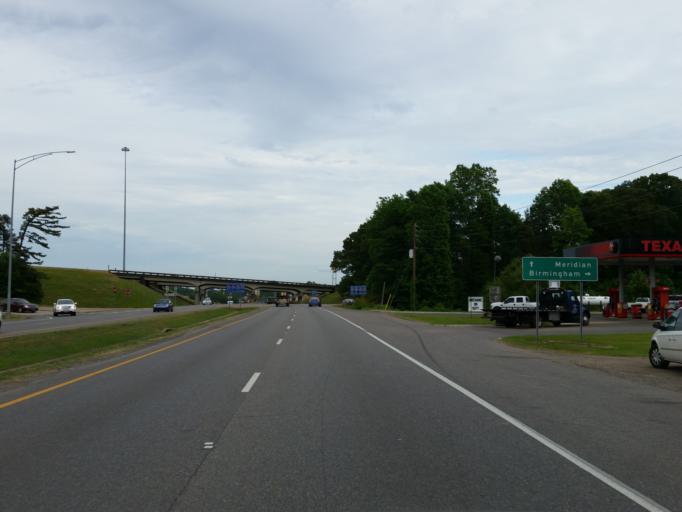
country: US
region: Alabama
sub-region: Tuscaloosa County
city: Holt
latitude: 33.1728
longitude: -87.4767
